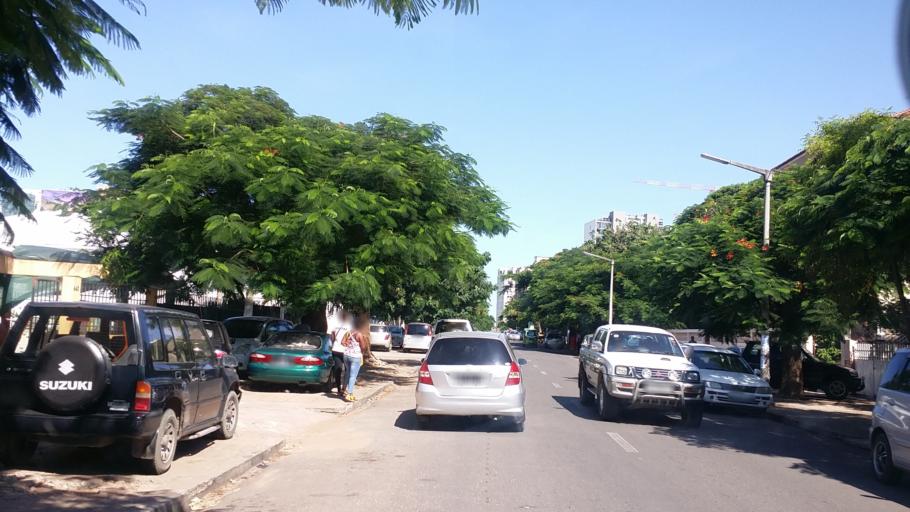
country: MZ
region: Maputo City
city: Maputo
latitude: -25.9734
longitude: 32.5896
